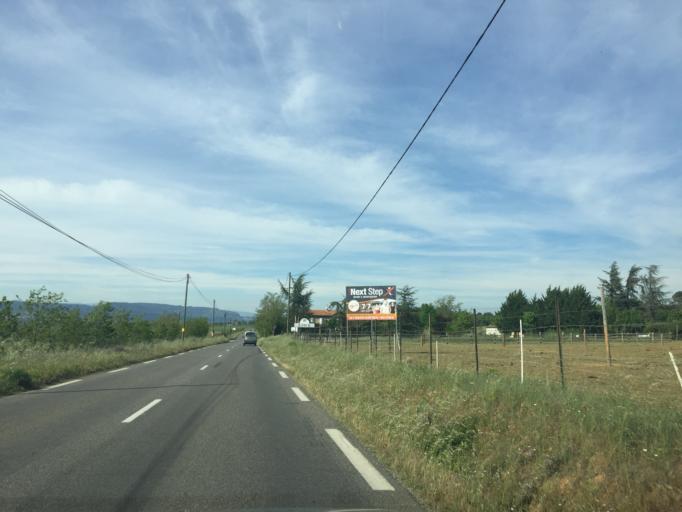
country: FR
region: Provence-Alpes-Cote d'Azur
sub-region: Departement du Var
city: Vinon-sur-Verdon
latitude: 43.7513
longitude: 5.8042
